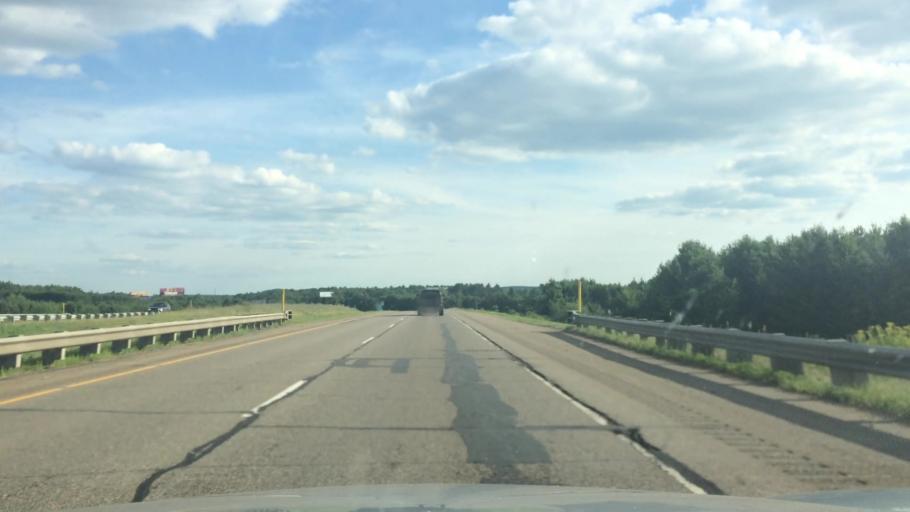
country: US
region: Wisconsin
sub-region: Lincoln County
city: Merrill
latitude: 45.1574
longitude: -89.6442
